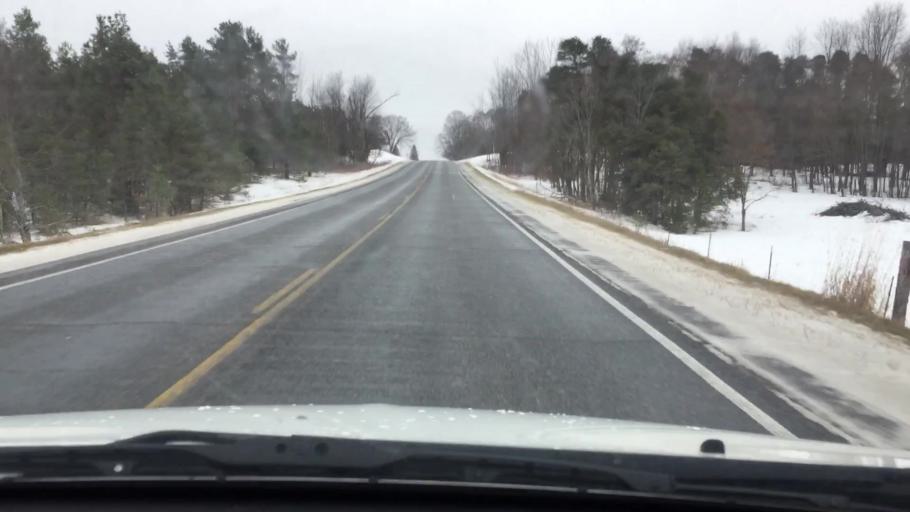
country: US
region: Michigan
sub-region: Wexford County
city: Cadillac
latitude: 44.0860
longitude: -85.4442
